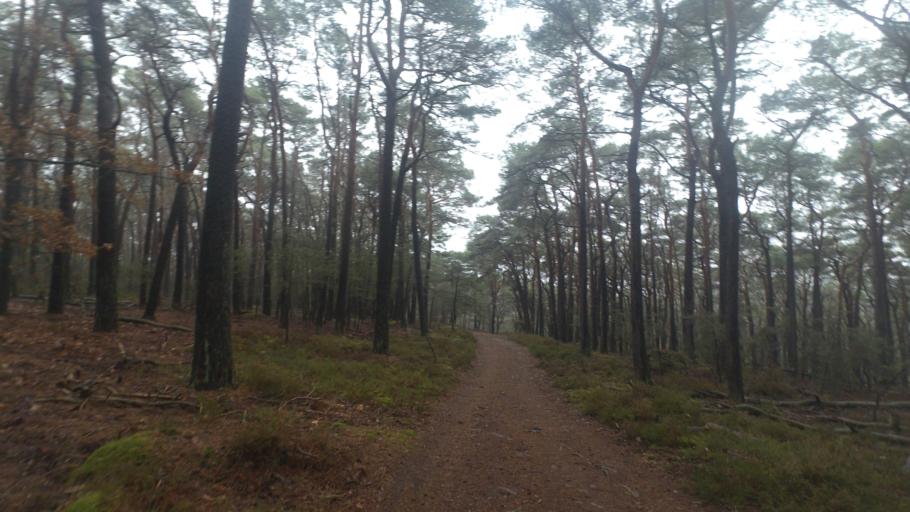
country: DE
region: Rheinland-Pfalz
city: Neustadt
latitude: 49.3899
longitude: 8.1375
